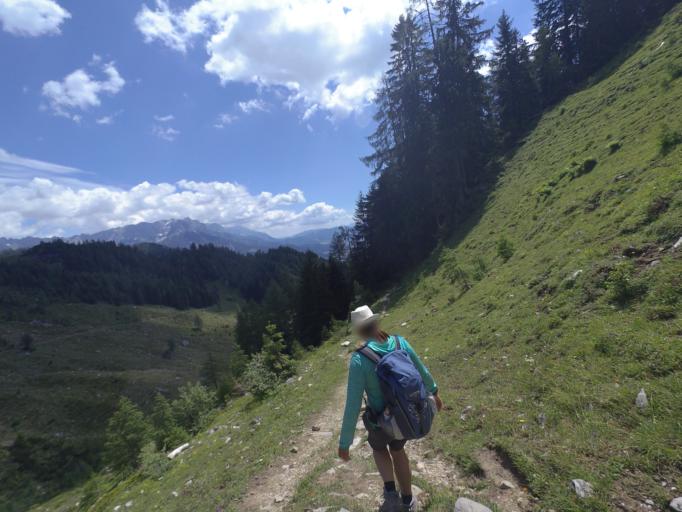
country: AT
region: Salzburg
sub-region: Politischer Bezirk Zell am See
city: Leogang
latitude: 47.4651
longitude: 12.7733
